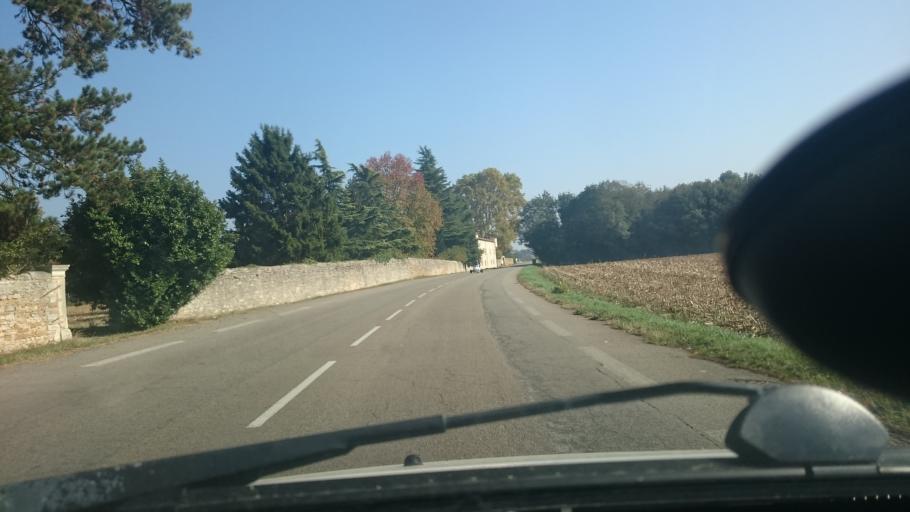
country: FR
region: Rhone-Alpes
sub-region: Departement de l'Ain
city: Trevoux
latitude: 45.9434
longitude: 4.7471
